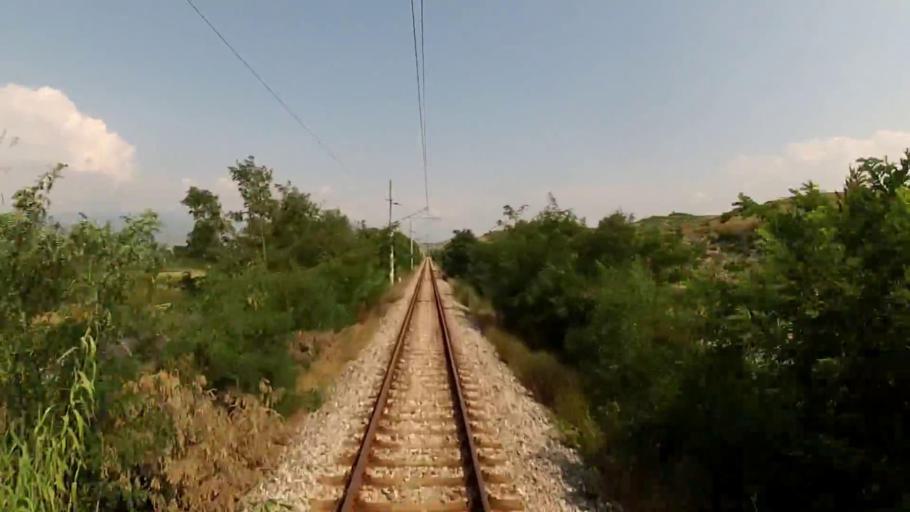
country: BG
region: Blagoevgrad
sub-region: Obshtina Strumyani
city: Strumyani
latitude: 41.6126
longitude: 23.2222
